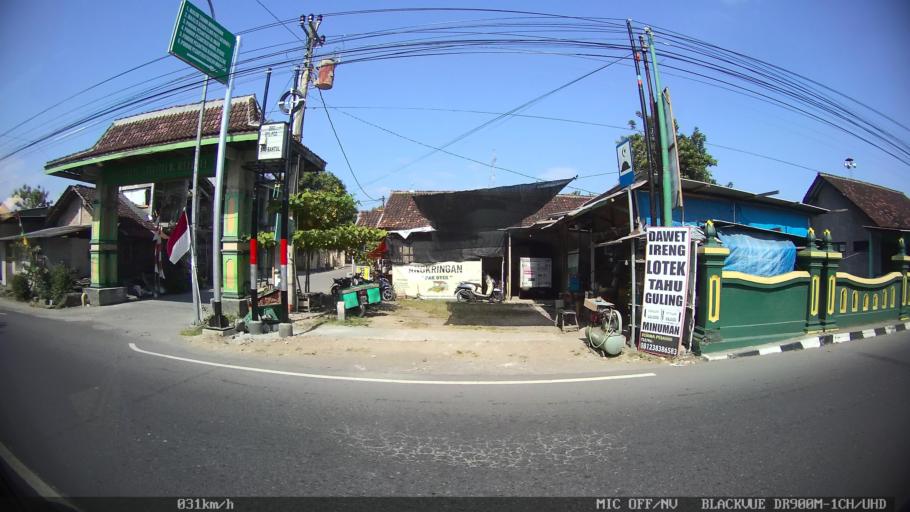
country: ID
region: Daerah Istimewa Yogyakarta
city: Sewon
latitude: -7.8745
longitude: 110.3924
